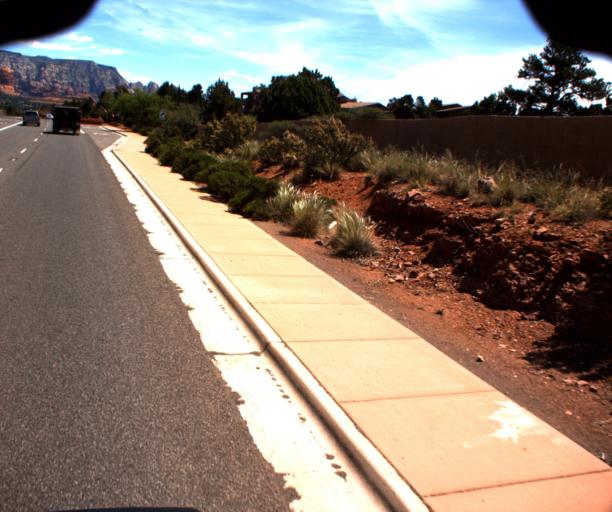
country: US
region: Arizona
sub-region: Yavapai County
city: West Sedona
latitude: 34.8519
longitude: -111.8261
